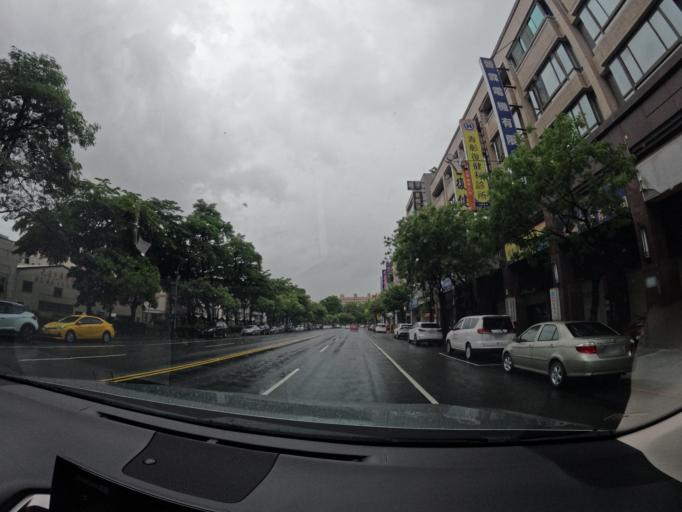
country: TW
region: Kaohsiung
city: Kaohsiung
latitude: 22.6598
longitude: 120.3271
